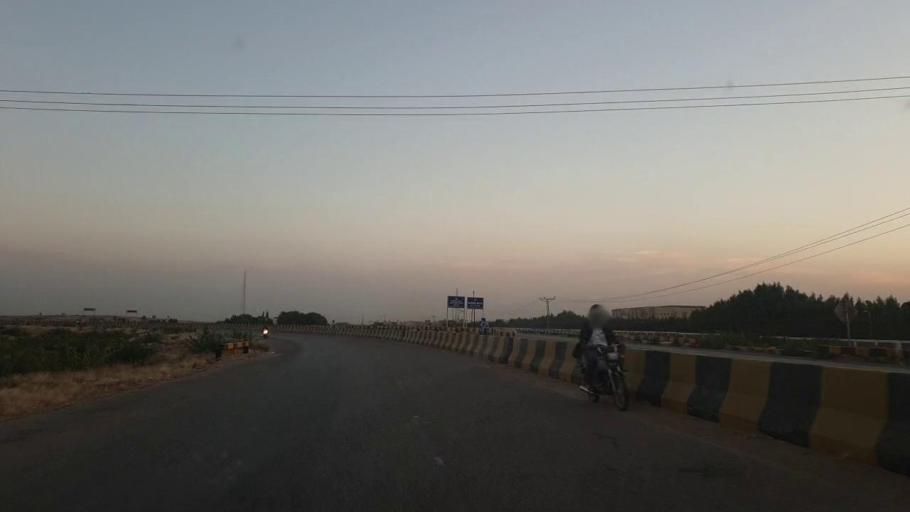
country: PK
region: Sindh
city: Jamshoro
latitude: 25.4064
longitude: 68.2673
